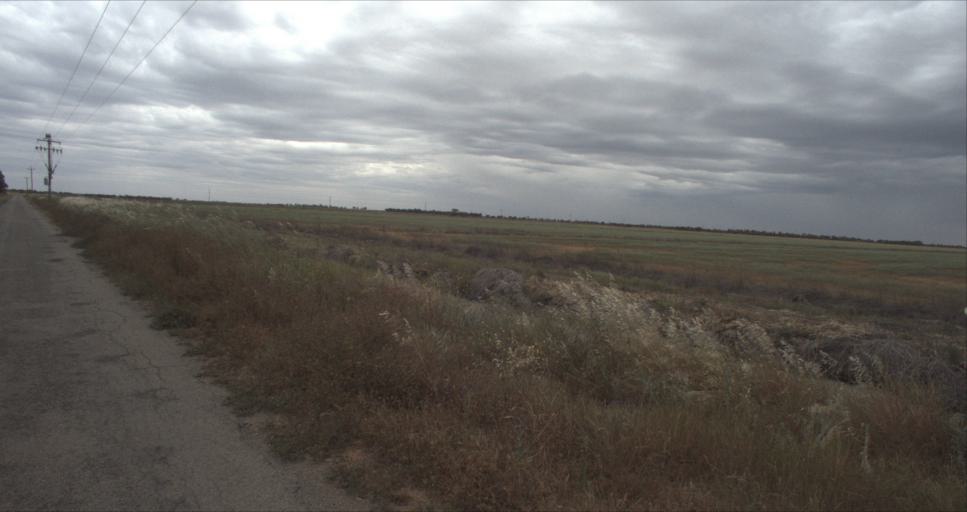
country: AU
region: New South Wales
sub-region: Leeton
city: Leeton
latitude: -34.4313
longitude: 146.3366
